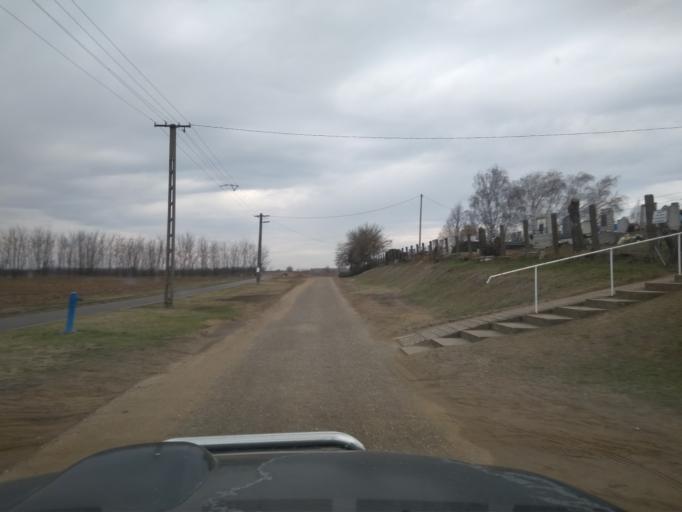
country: HU
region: Szabolcs-Szatmar-Bereg
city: Kemecse
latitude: 48.0556
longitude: 21.7967
